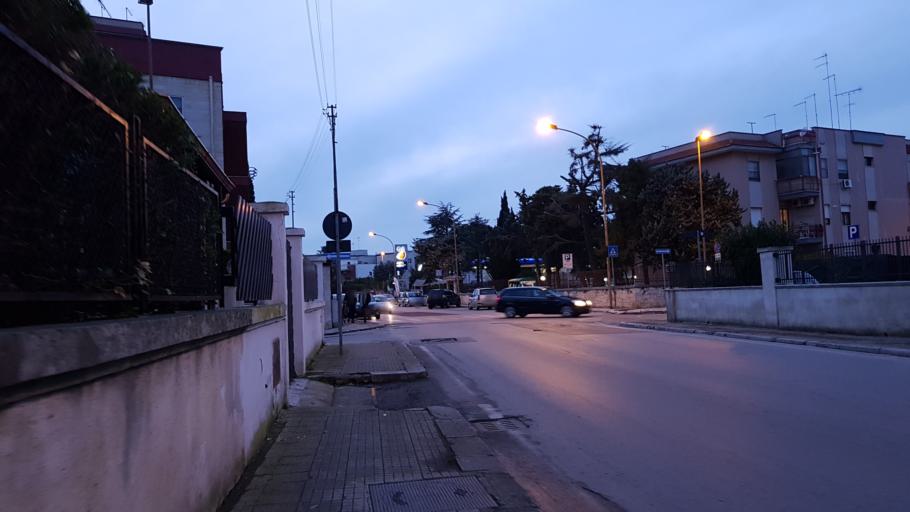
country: IT
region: Apulia
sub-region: Provincia di Brindisi
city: Brindisi
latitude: 40.6487
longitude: 17.9416
